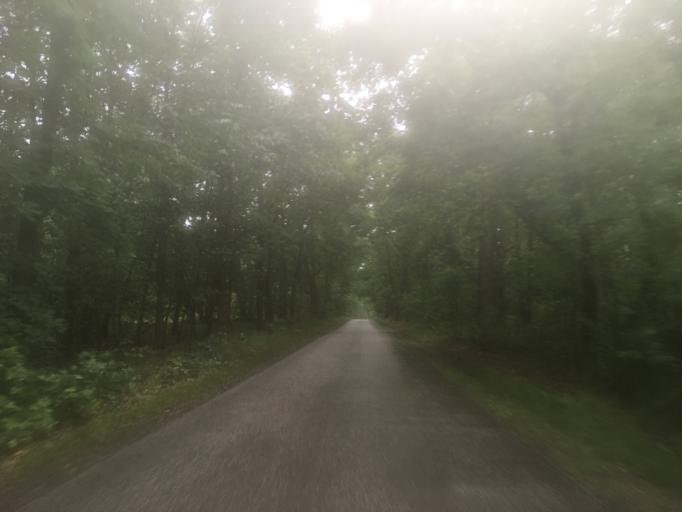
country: DE
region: Brandenburg
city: Zehdenick
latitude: 53.0313
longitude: 13.2970
